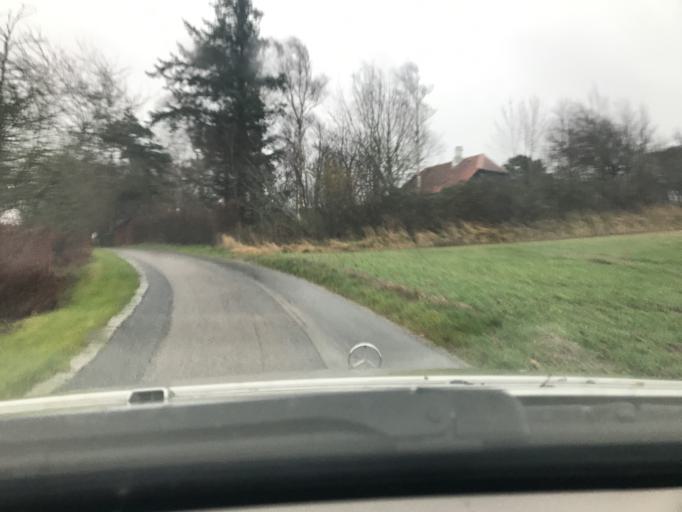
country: DK
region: South Denmark
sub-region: Sonderborg Kommune
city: Horuphav
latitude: 54.8757
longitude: 9.8764
